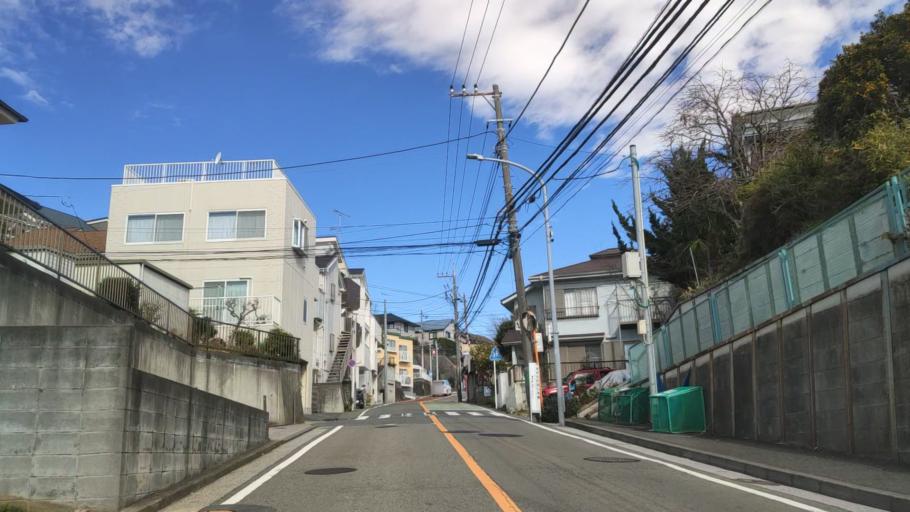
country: JP
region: Kanagawa
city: Yokohama
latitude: 35.4687
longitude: 139.5846
